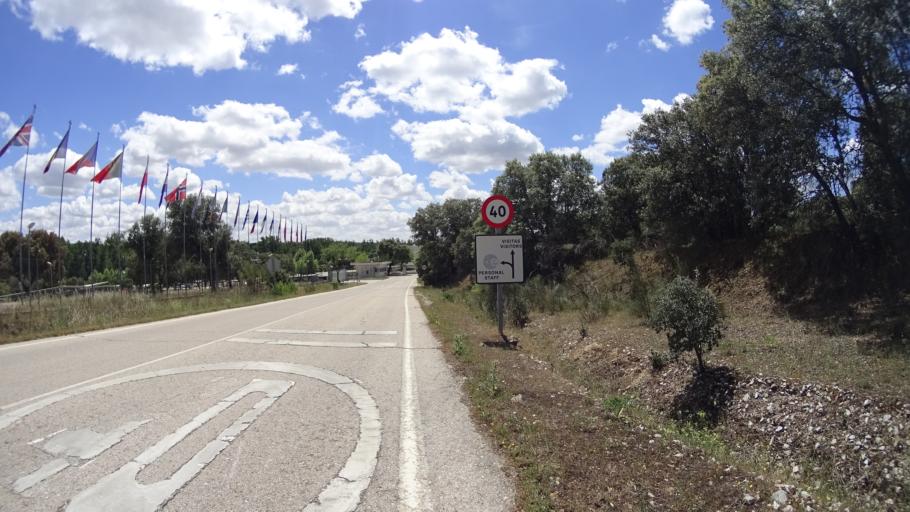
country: ES
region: Madrid
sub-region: Provincia de Madrid
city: Villanueva del Pardillo
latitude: 40.4456
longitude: -3.9531
